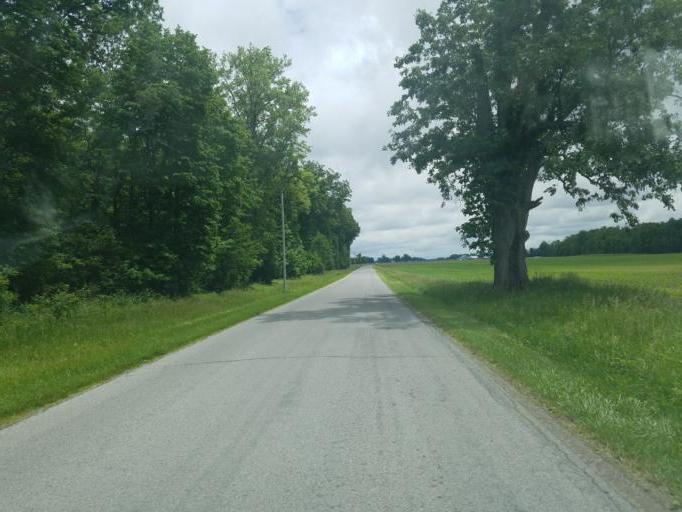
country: US
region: Ohio
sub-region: Crawford County
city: Bucyrus
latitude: 40.7757
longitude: -83.0404
